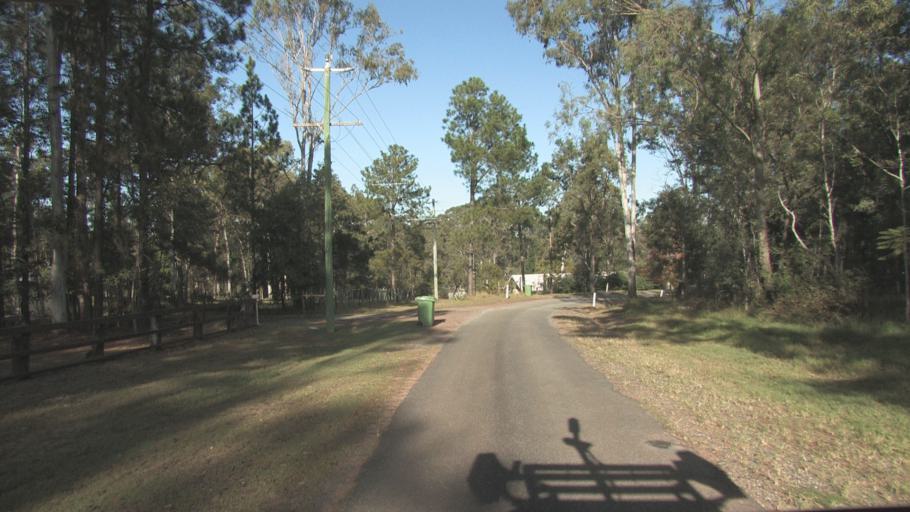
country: AU
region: Queensland
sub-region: Logan
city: Park Ridge South
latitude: -27.7475
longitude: 153.0441
